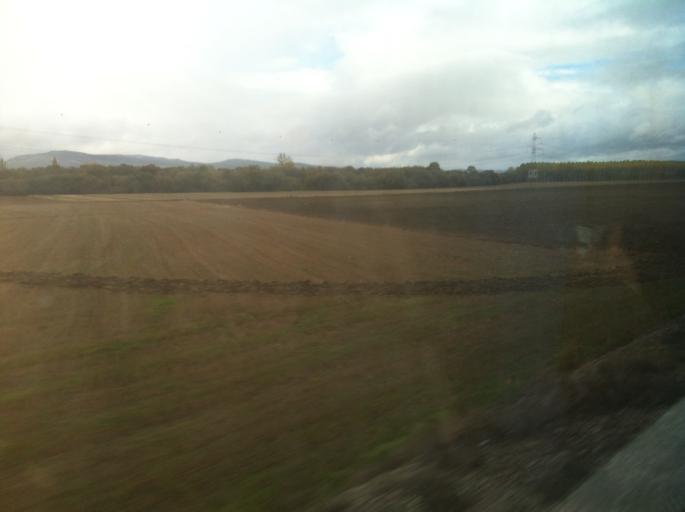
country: ES
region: Basque Country
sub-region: Provincia de Alava
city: Gasteiz / Vitoria
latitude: 42.8447
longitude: -2.7653
